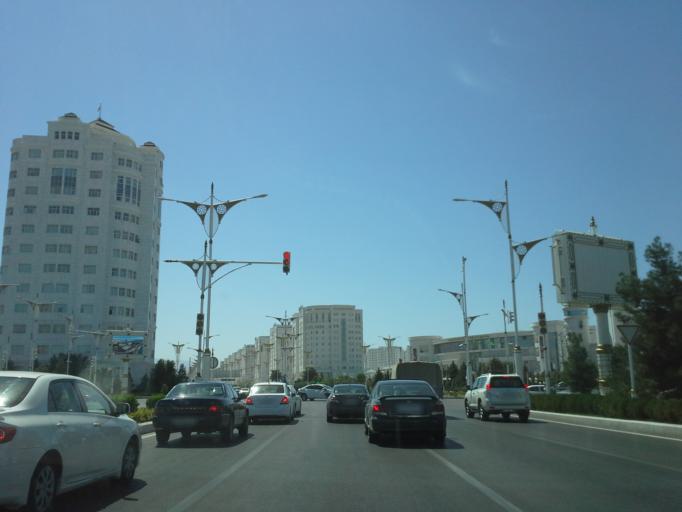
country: TM
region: Ahal
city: Ashgabat
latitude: 37.9160
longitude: 58.3724
